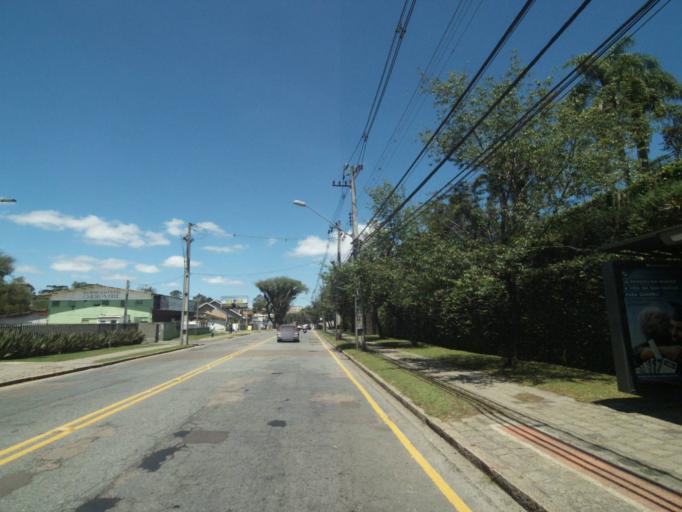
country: BR
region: Parana
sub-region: Curitiba
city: Curitiba
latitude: -25.3889
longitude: -49.2676
